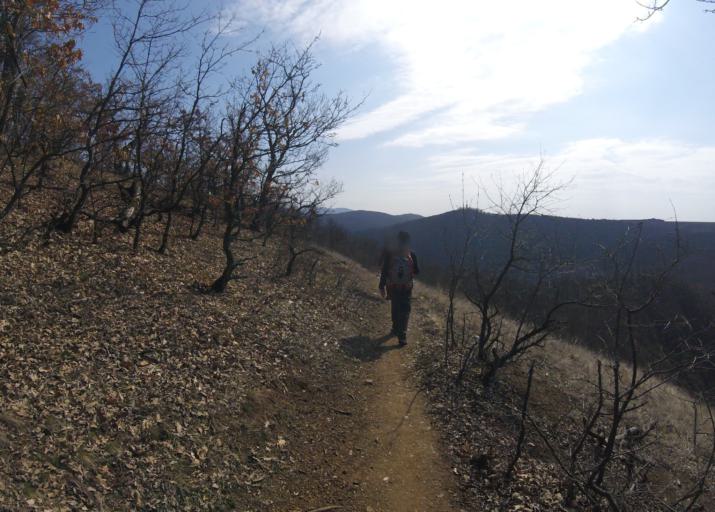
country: HU
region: Heves
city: Belapatfalva
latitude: 47.9941
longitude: 20.3289
